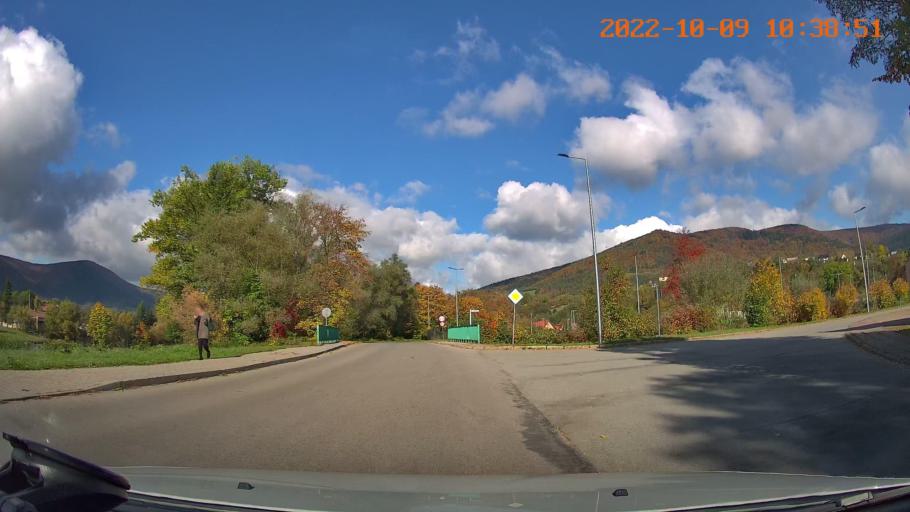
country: PL
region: Lesser Poland Voivodeship
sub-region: Powiat limanowski
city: Mszana Dolna
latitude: 49.6764
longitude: 20.0781
